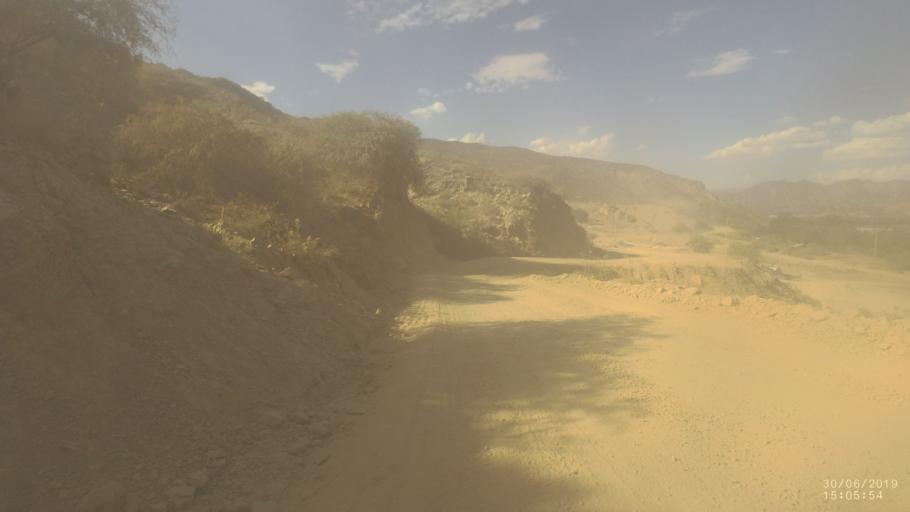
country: BO
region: Cochabamba
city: Irpa Irpa
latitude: -17.7323
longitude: -66.3142
